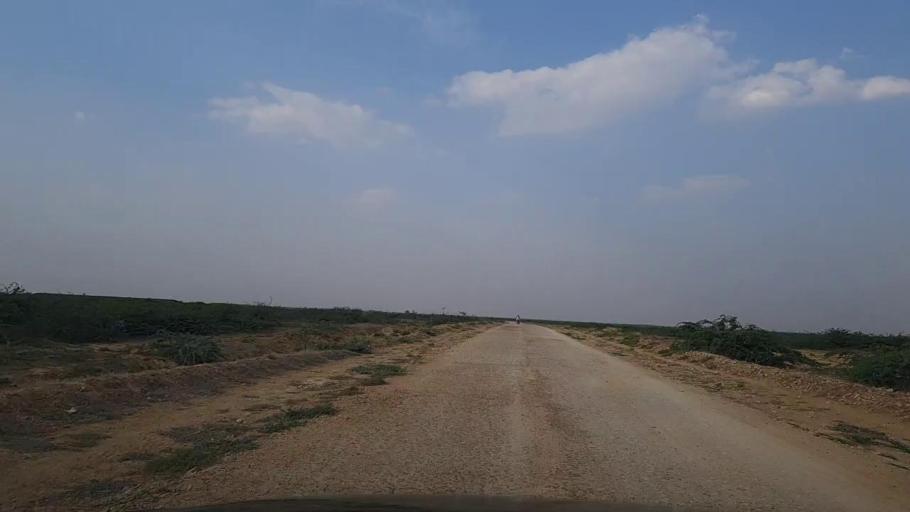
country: PK
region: Sindh
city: Gharo
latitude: 24.8196
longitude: 67.7437
